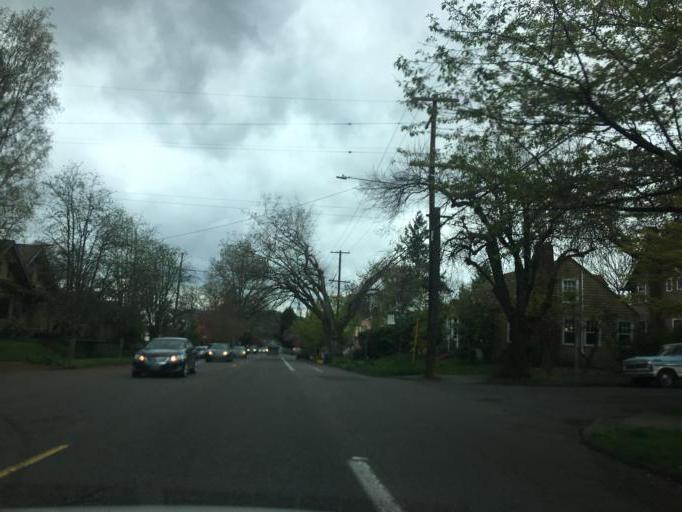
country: US
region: Oregon
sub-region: Multnomah County
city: Portland
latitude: 45.5265
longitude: -122.6277
